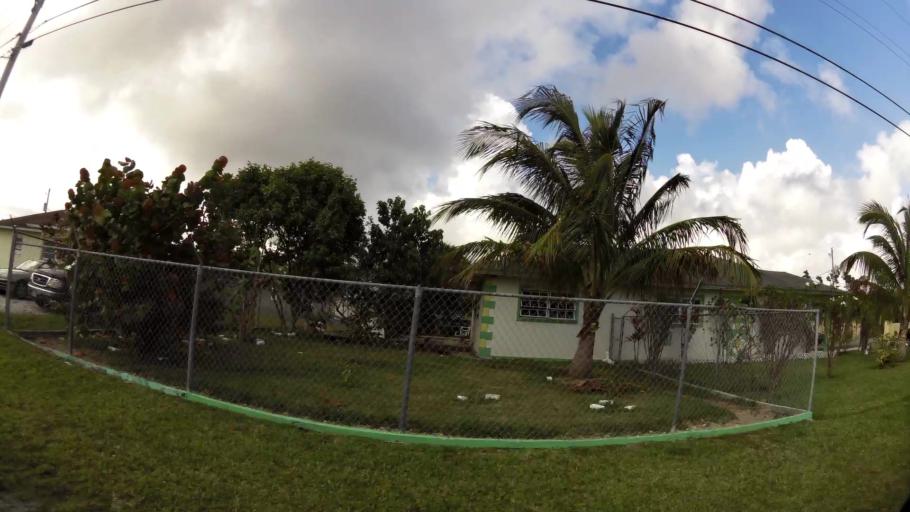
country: BS
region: Freeport
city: Freeport
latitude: 26.5276
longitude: -78.7077
